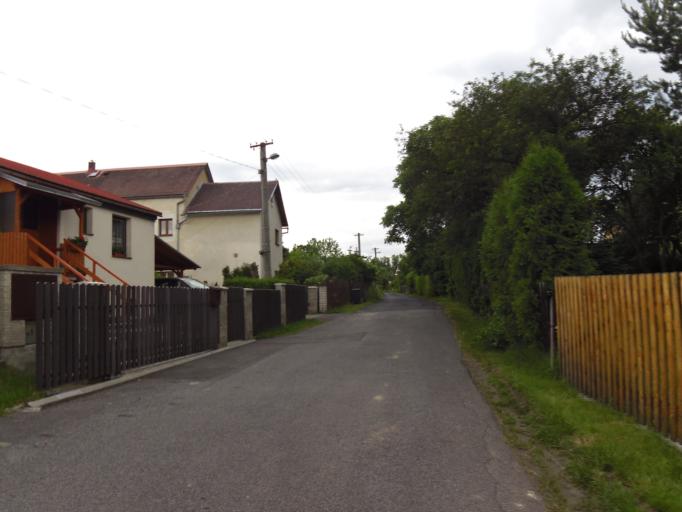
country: CZ
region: Ustecky
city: Varnsdorf
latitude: 50.8946
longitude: 14.6226
